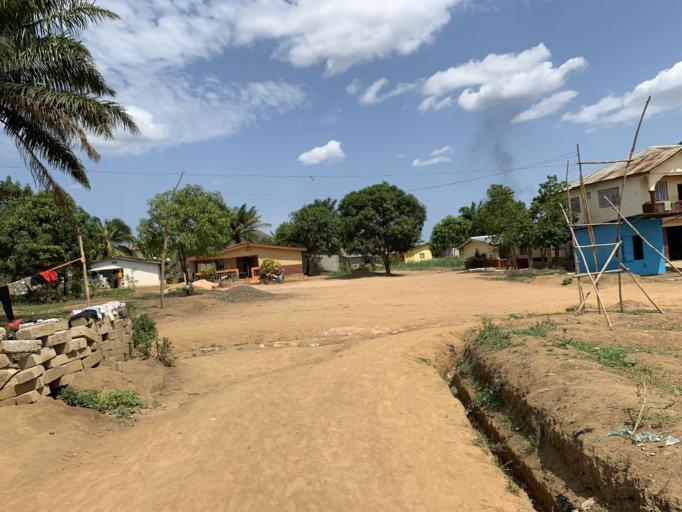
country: SL
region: Western Area
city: Waterloo
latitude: 8.3298
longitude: -13.0443
